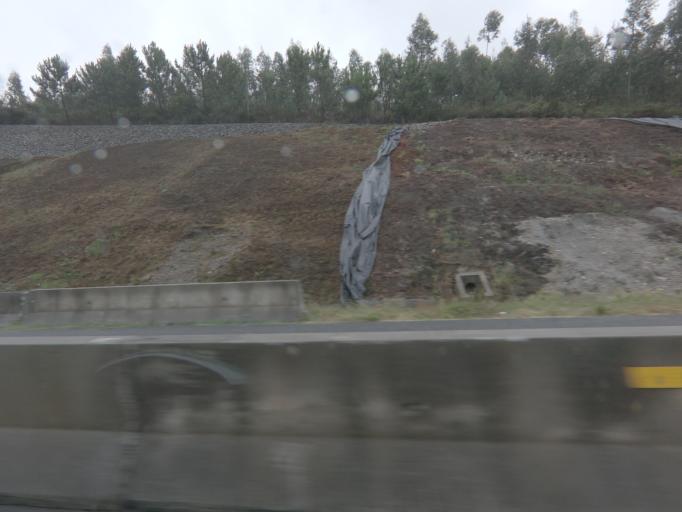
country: PT
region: Porto
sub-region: Valongo
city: Valongo
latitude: 41.2024
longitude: -8.5239
